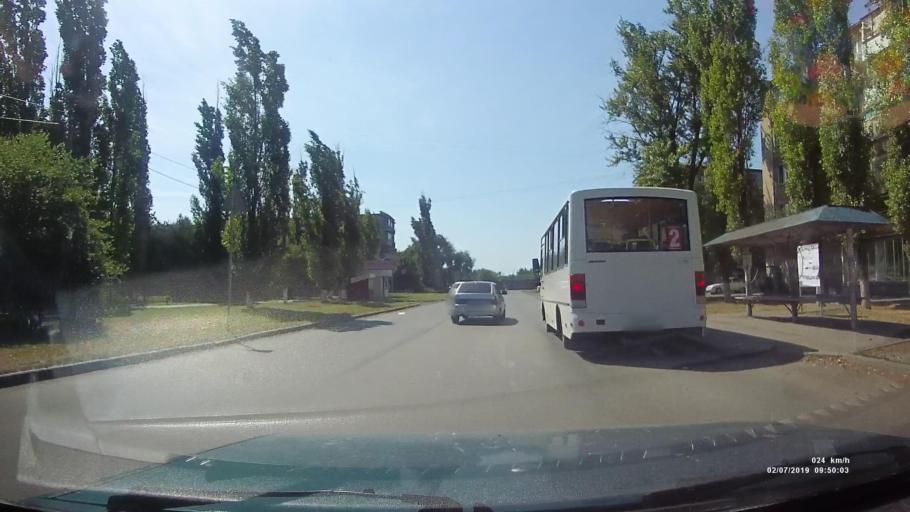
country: RU
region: Rostov
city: Azov
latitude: 47.1028
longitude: 39.4028
